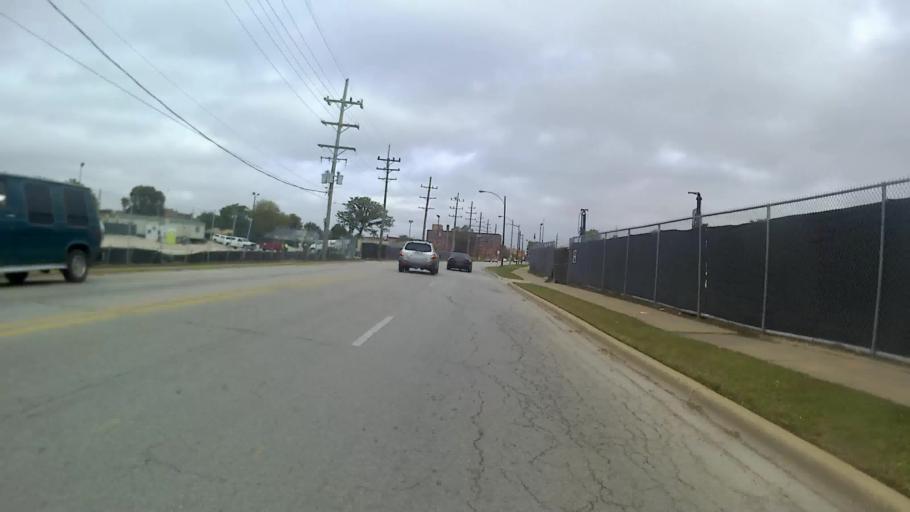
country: US
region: Illinois
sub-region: Kane County
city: Aurora
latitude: 41.7520
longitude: -88.3259
